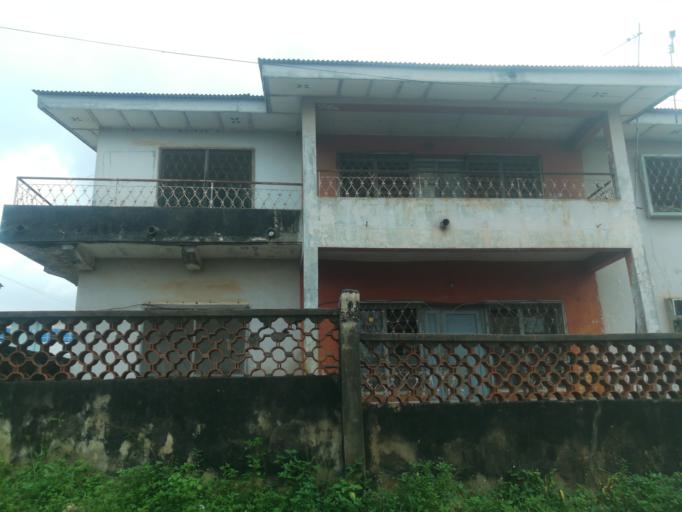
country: NG
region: Oyo
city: Ibadan
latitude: 7.3523
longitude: 3.8727
